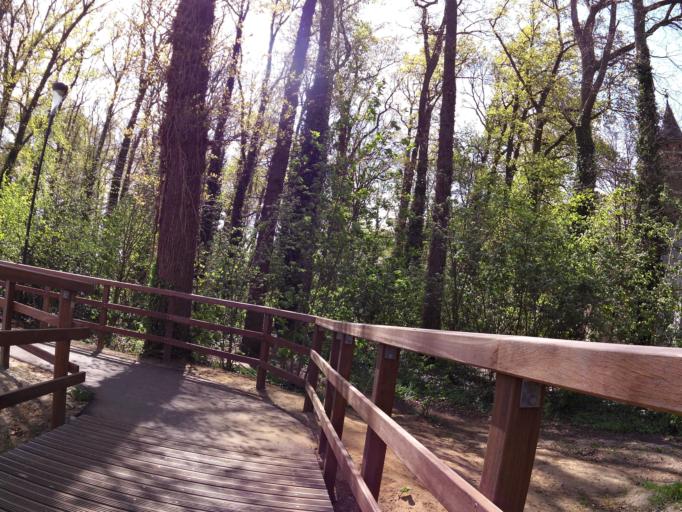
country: NL
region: North Brabant
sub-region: Gemeente Schijndel
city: Schijndel
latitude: 51.6633
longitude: 5.4103
